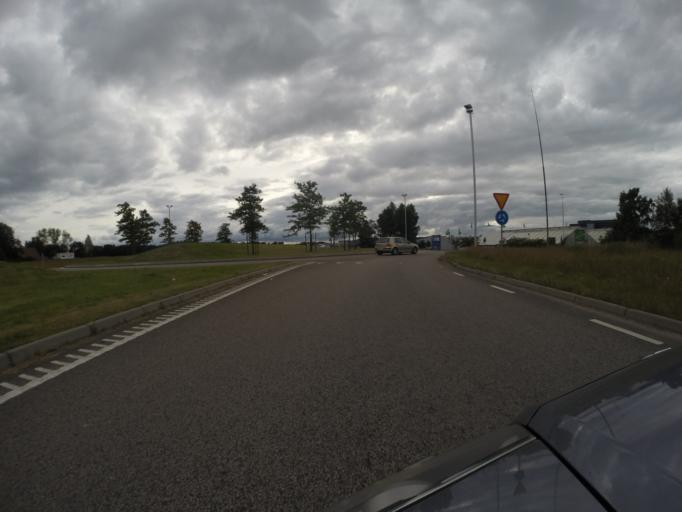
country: SE
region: Skane
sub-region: Helsingborg
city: Odakra
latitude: 56.0917
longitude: 12.7708
